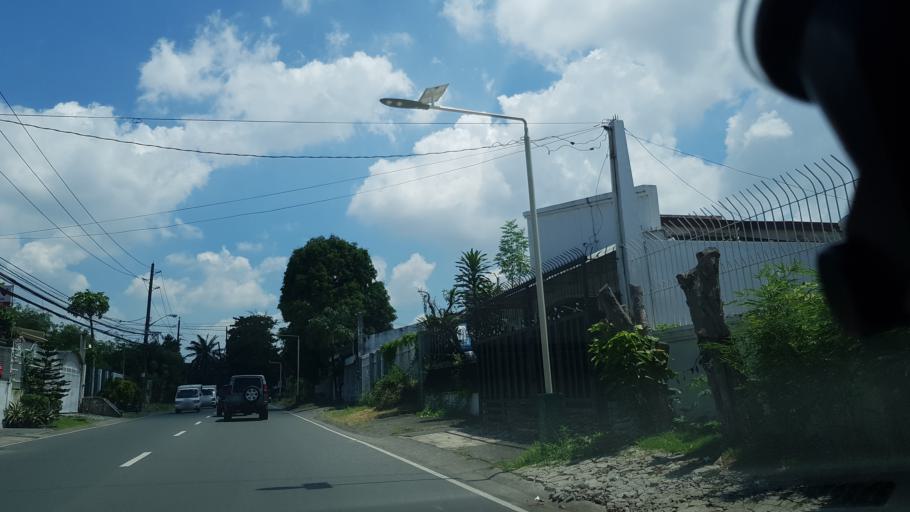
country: PH
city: Sambayanihan People's Village
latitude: 14.4514
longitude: 120.9988
